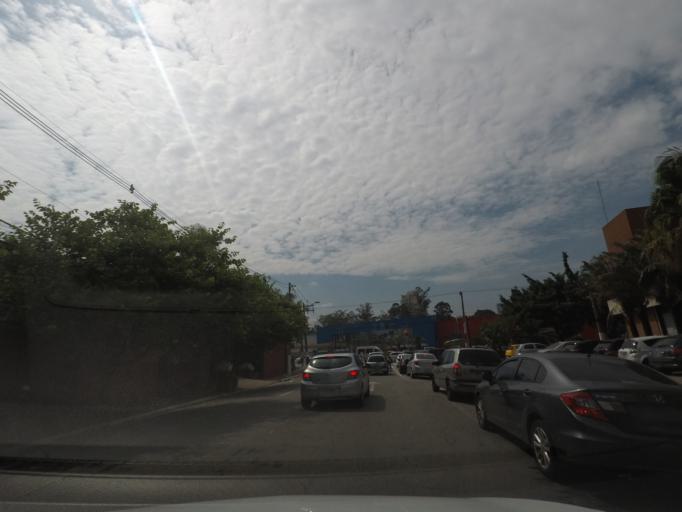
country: BR
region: Sao Paulo
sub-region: Sao Paulo
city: Sao Paulo
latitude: -23.5896
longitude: -46.6209
